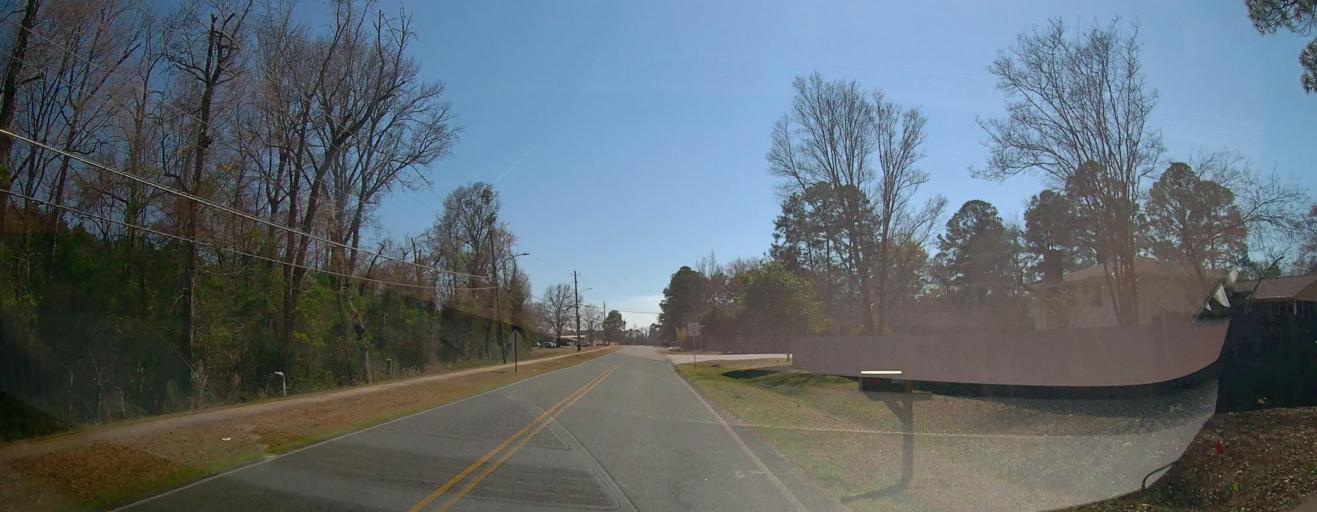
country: US
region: Georgia
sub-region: Houston County
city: Perry
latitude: 32.4622
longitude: -83.7113
